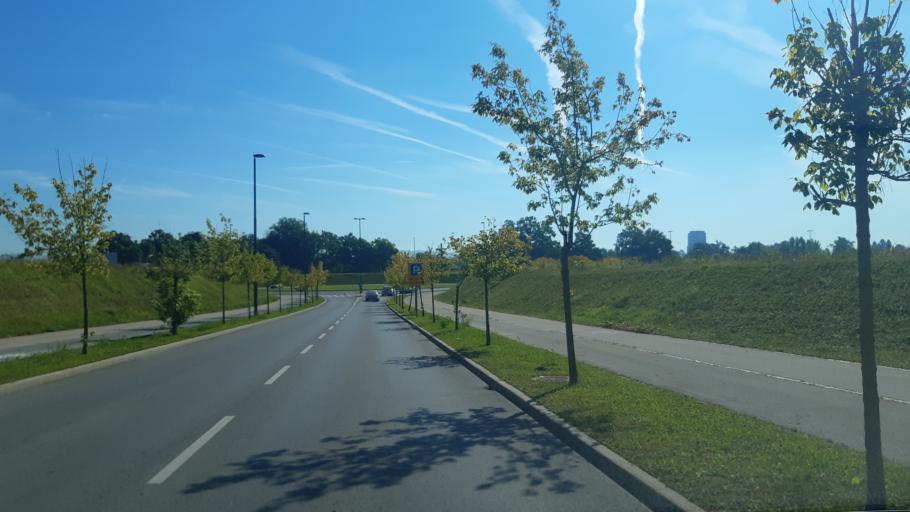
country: SI
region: Ljubljana
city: Ljubljana
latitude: 46.0755
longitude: 14.5228
